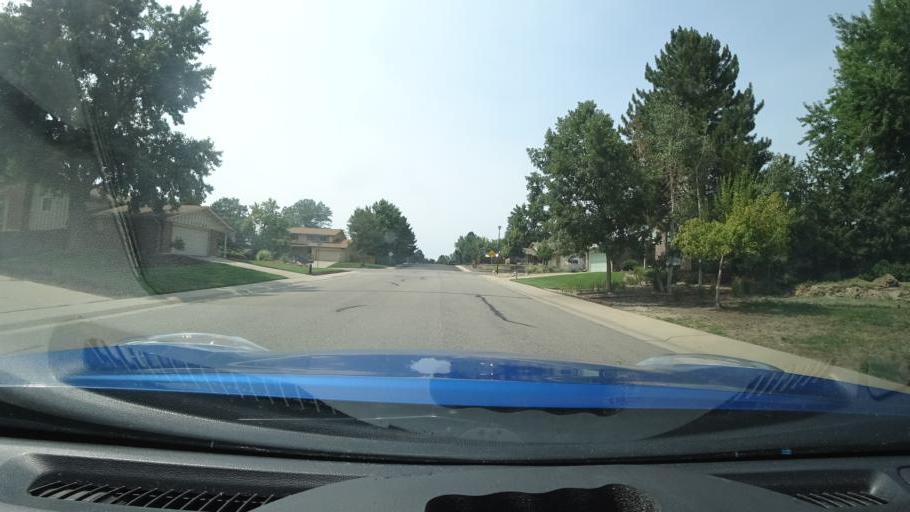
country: US
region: Colorado
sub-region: Adams County
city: Aurora
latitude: 39.6695
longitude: -104.8577
